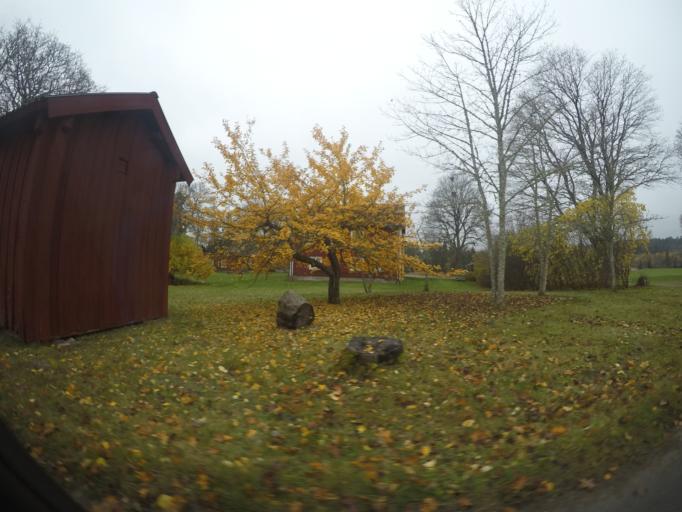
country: SE
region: Vaestmanland
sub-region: Surahammars Kommun
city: Ramnas
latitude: 59.7299
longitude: 16.1028
